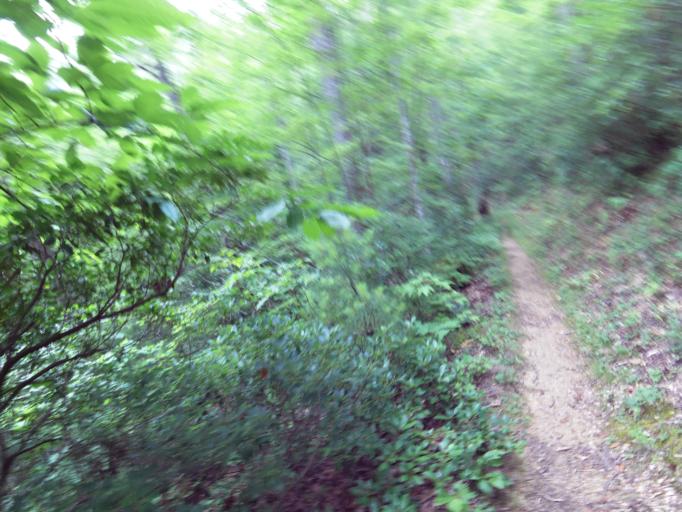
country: US
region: Tennessee
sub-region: Blount County
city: Wildwood
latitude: 35.6458
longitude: -83.8105
